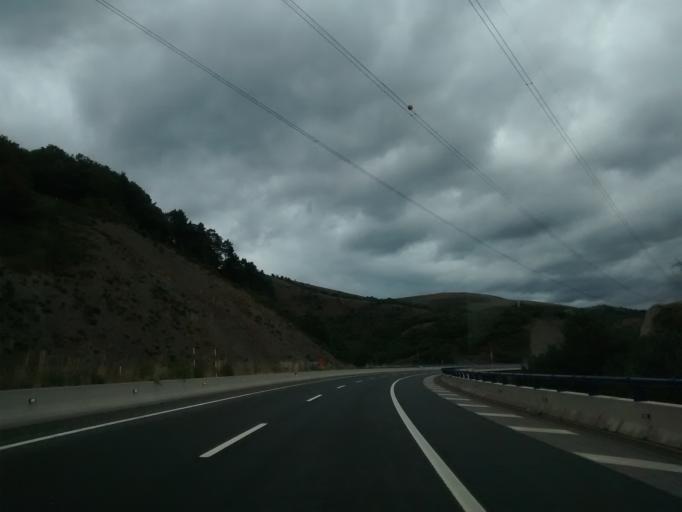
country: ES
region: Cantabria
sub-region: Provincia de Cantabria
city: Reinosa
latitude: 43.0281
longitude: -4.1121
